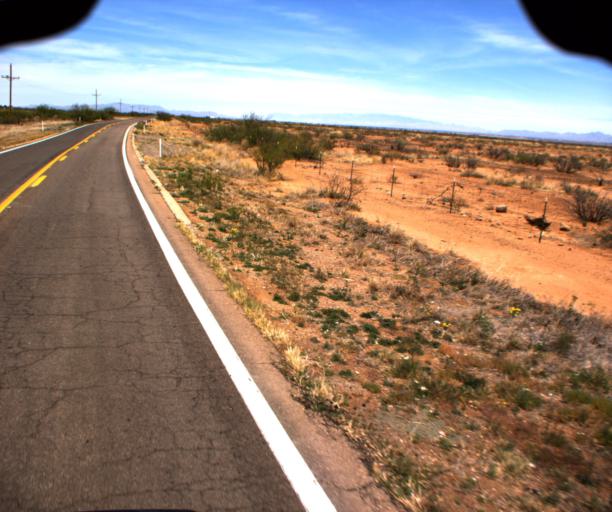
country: US
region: Arizona
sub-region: Cochise County
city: Tombstone
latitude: 31.9100
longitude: -109.8157
